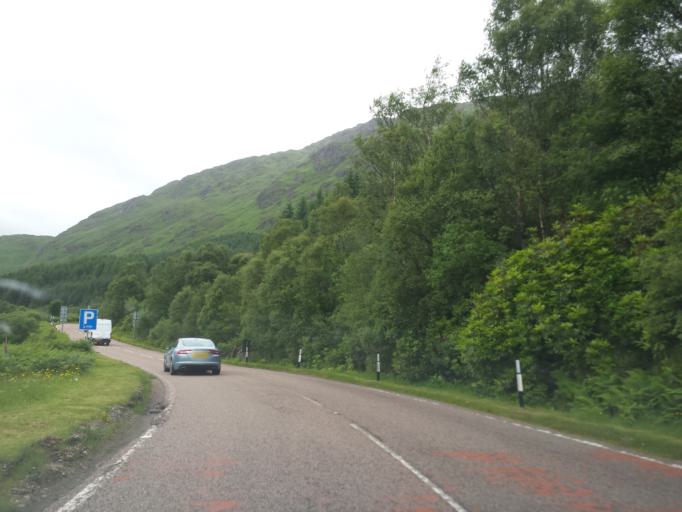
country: GB
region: Scotland
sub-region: Highland
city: Fort William
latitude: 56.8749
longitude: -5.4578
